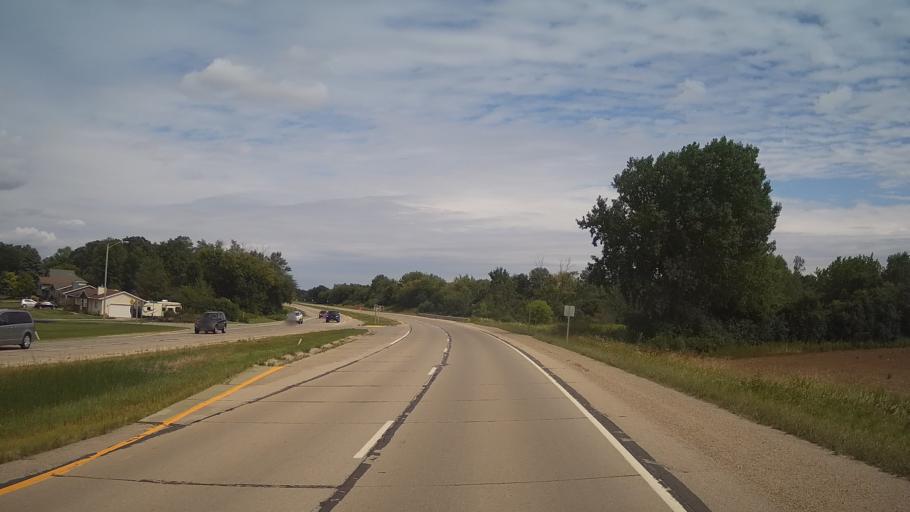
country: US
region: Wisconsin
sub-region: Winnebago County
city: Oshkosh
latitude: 44.0298
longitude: -88.6164
